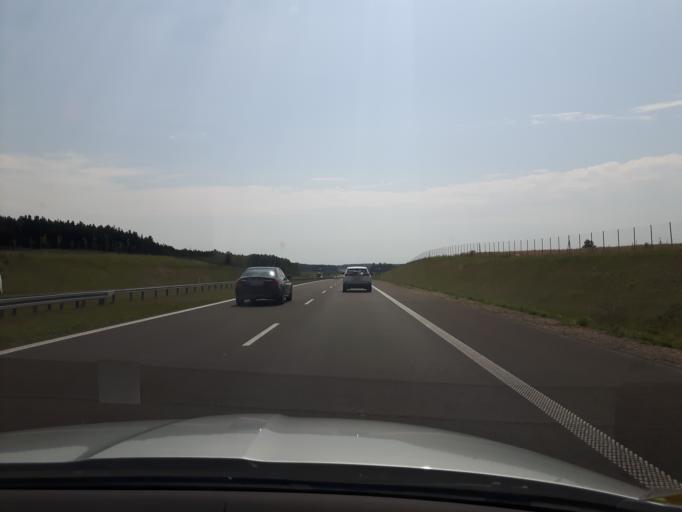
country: PL
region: Warmian-Masurian Voivodeship
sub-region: Powiat nidzicki
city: Nidzica
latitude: 53.3205
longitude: 20.4389
